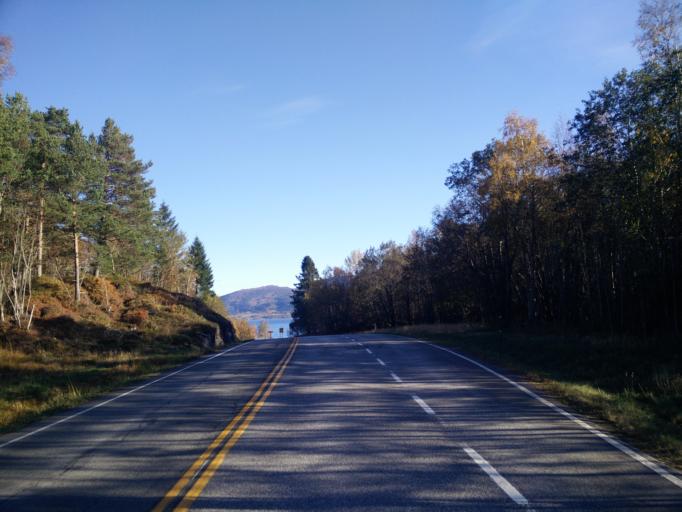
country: NO
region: More og Romsdal
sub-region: Tingvoll
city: Tingvoll
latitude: 63.0519
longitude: 8.1191
